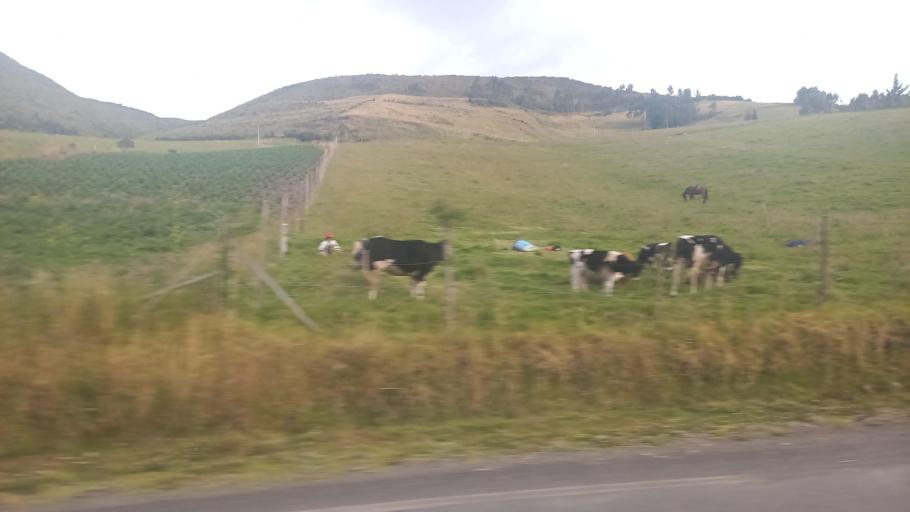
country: EC
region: Pichincha
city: Cayambe
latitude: 0.1040
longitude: -78.0809
